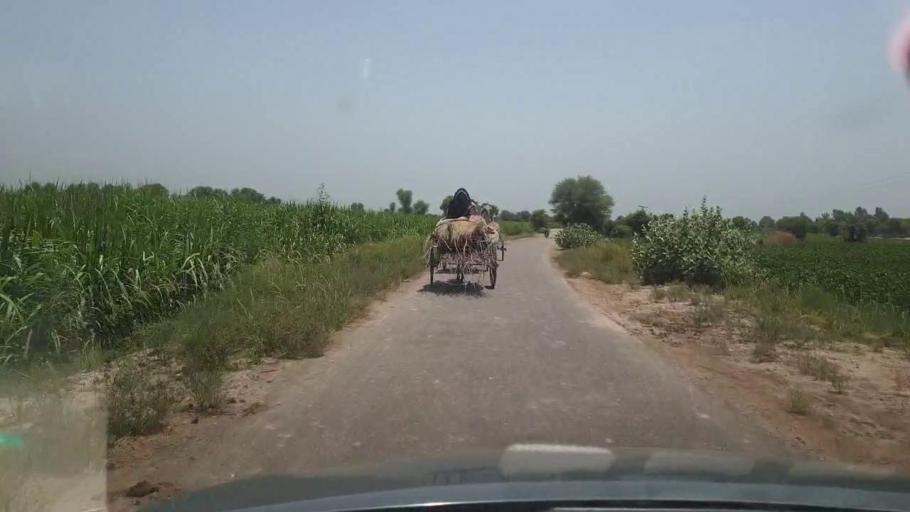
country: PK
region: Sindh
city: Hingorja
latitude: 27.2275
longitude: 68.3180
